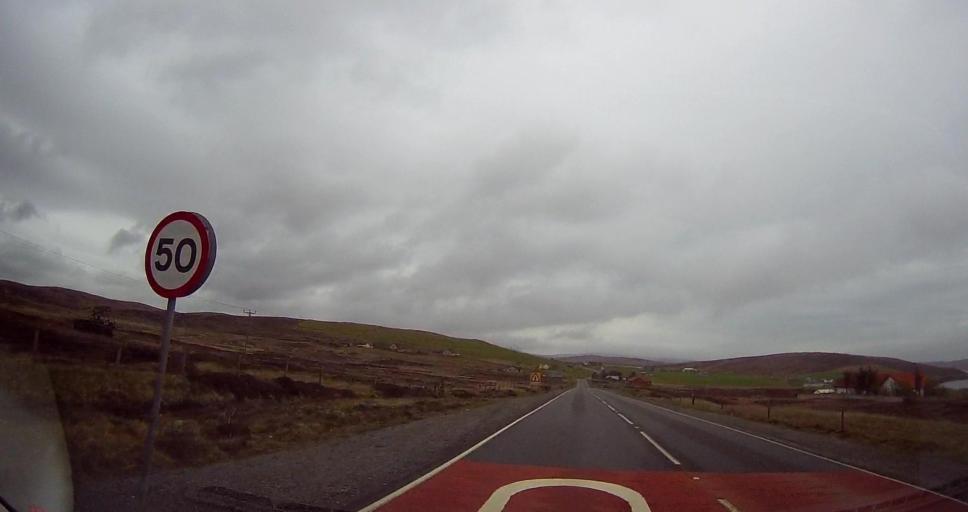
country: GB
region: Scotland
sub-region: Shetland Islands
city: Lerwick
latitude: 60.2313
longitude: -1.2365
